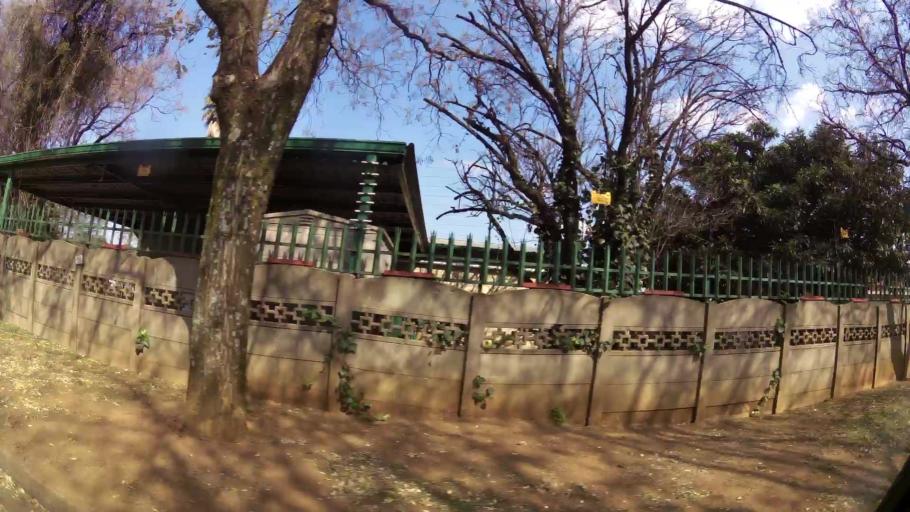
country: ZA
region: Gauteng
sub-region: Ekurhuleni Metropolitan Municipality
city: Germiston
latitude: -26.1894
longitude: 28.2019
